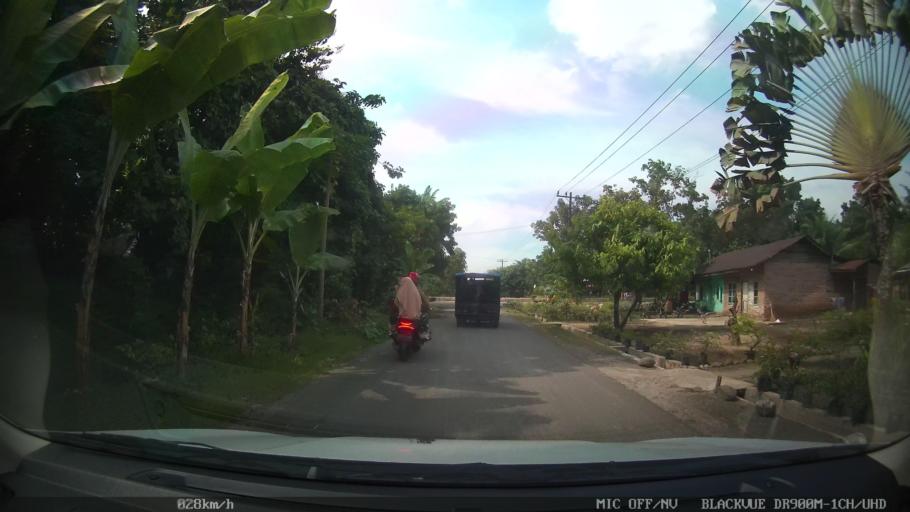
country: ID
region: North Sumatra
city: Binjai
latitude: 3.6502
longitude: 98.5179
